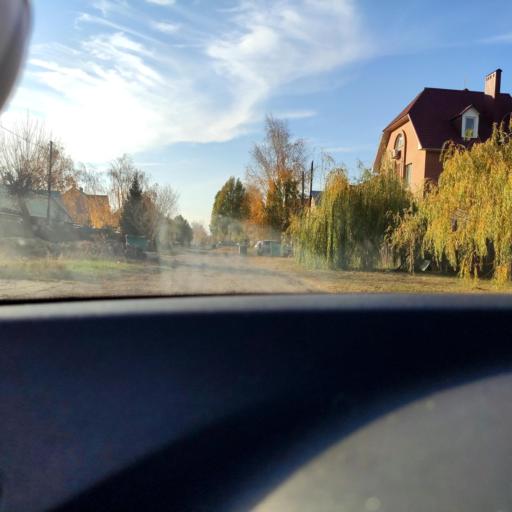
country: RU
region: Samara
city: Petra-Dubrava
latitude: 53.2572
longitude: 50.3291
